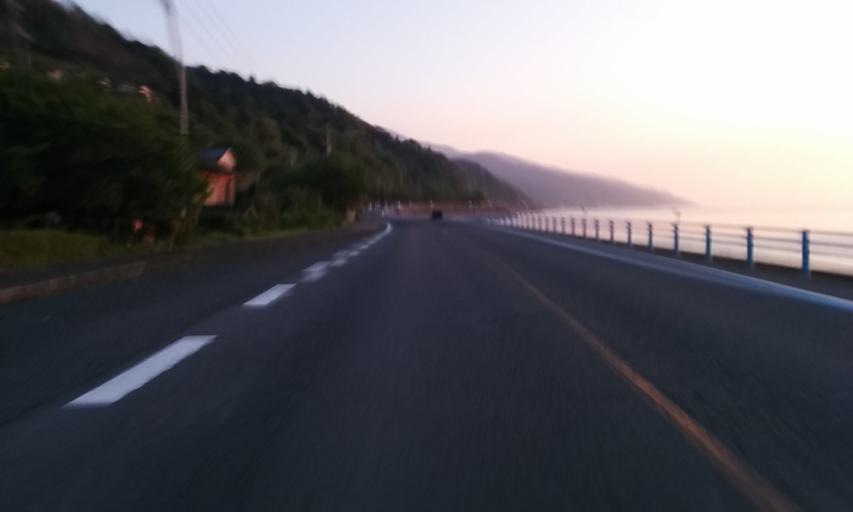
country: JP
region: Ehime
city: Iyo
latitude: 33.6679
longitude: 132.6082
